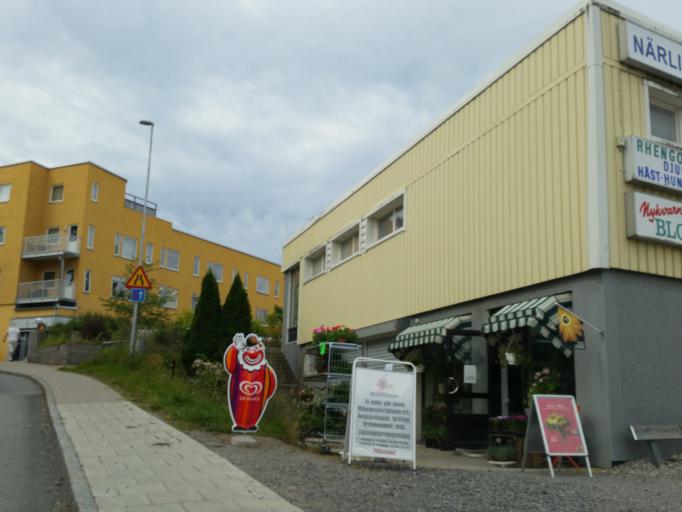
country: SE
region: Stockholm
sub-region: Nykvarns Kommun
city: Nykvarn
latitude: 59.1771
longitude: 17.4345
